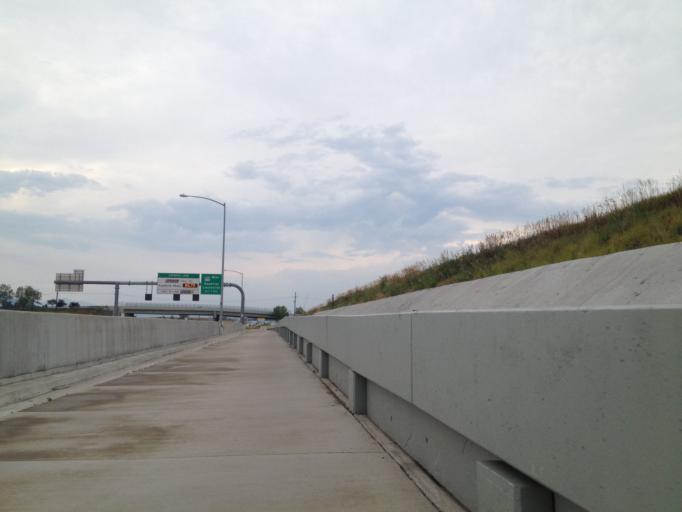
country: US
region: Colorado
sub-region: Boulder County
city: Superior
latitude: 39.9439
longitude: -105.1437
